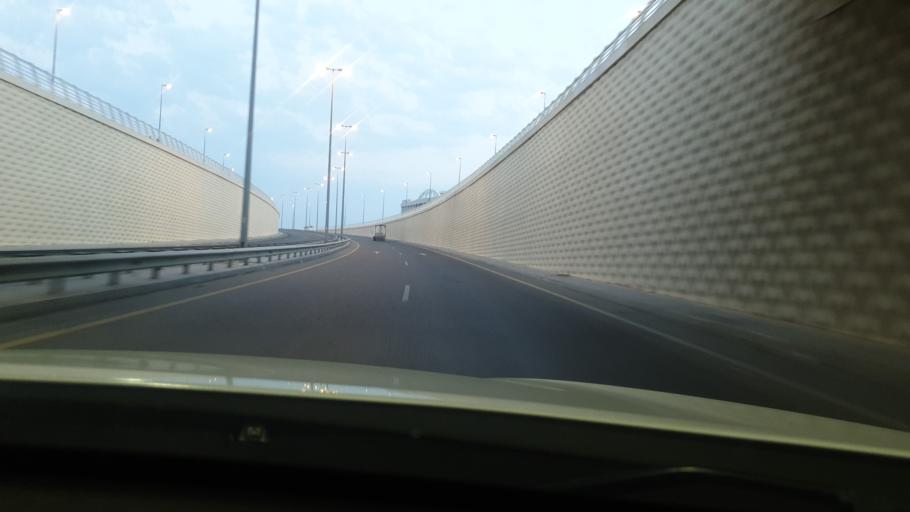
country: AZ
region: Baki
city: Bilajer
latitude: 40.5777
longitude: 50.0607
